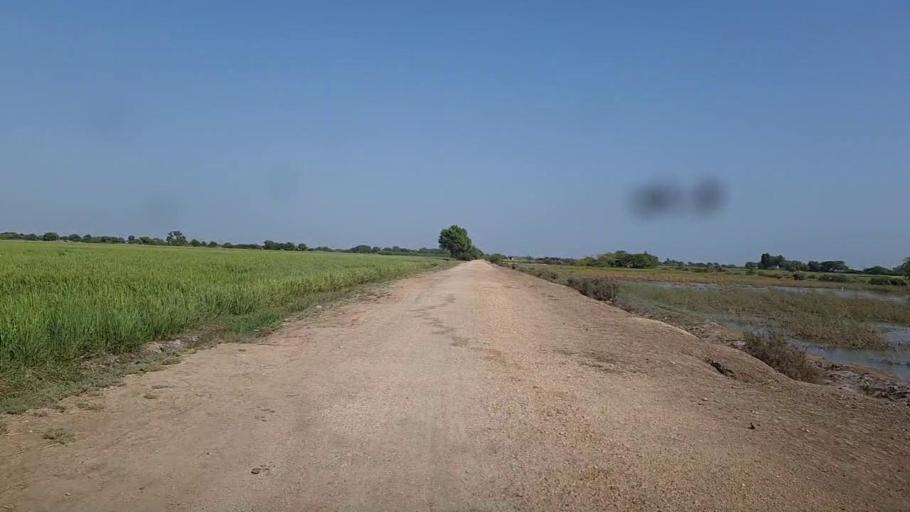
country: PK
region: Sindh
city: Kario
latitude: 24.7518
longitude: 68.4586
